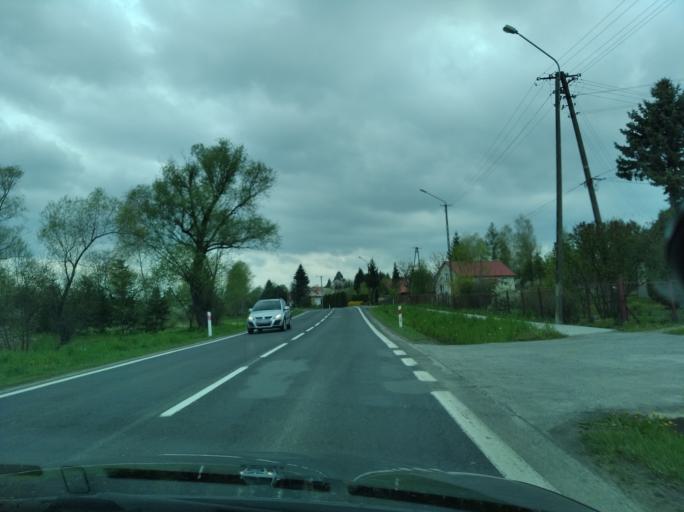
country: PL
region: Subcarpathian Voivodeship
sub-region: Powiat sanocki
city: Nowosielce-Gniewosz
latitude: 49.5594
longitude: 22.0932
